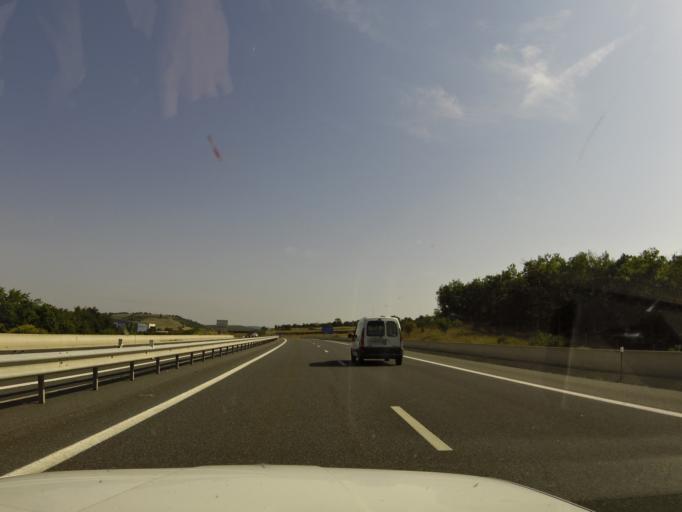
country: FR
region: Midi-Pyrenees
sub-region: Departement de l'Aveyron
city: Creissels
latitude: 44.1483
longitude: 3.0170
